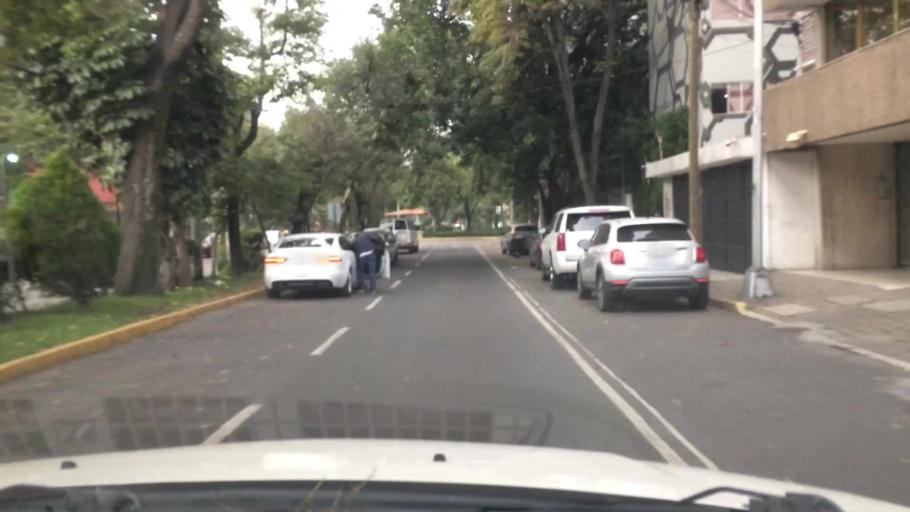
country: MX
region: Mexico City
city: Alvaro Obregon
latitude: 19.3560
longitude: -99.1876
